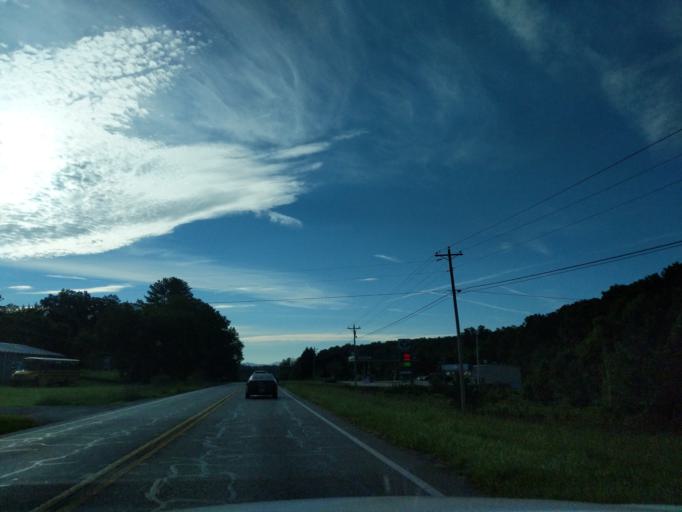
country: US
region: Georgia
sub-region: Fannin County
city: Blue Ridge
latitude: 34.8974
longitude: -84.3620
